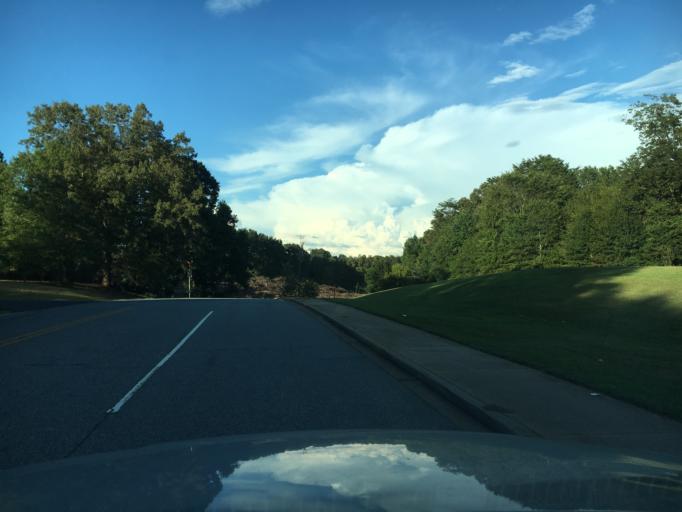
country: US
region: South Carolina
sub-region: Spartanburg County
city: Roebuck
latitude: 34.8850
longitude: -82.0041
